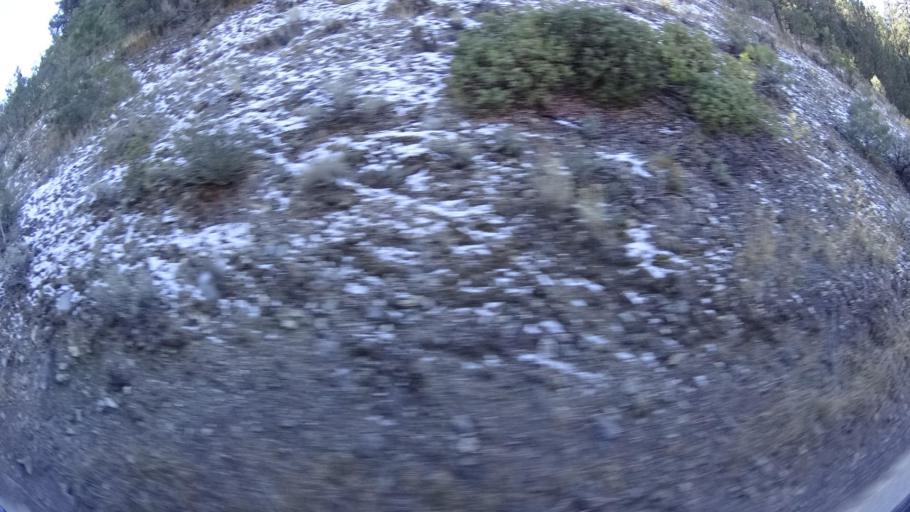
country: US
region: California
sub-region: Kern County
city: Pine Mountain Club
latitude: 34.8515
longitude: -119.1130
